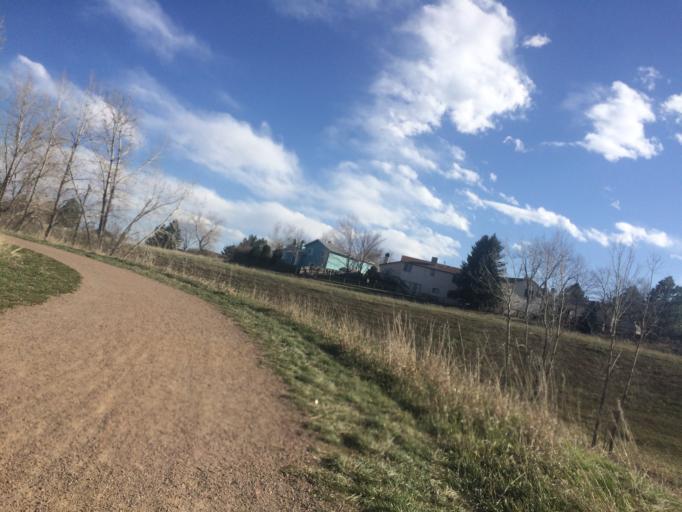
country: US
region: Colorado
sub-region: Boulder County
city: Louisville
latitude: 39.9825
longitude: -105.1479
